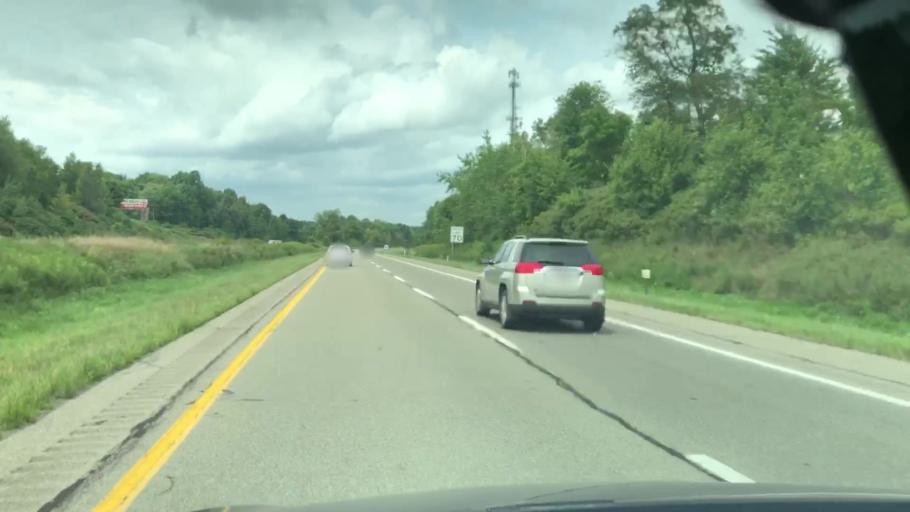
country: US
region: Pennsylvania
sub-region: Crawford County
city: Meadville
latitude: 41.7227
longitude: -80.2035
